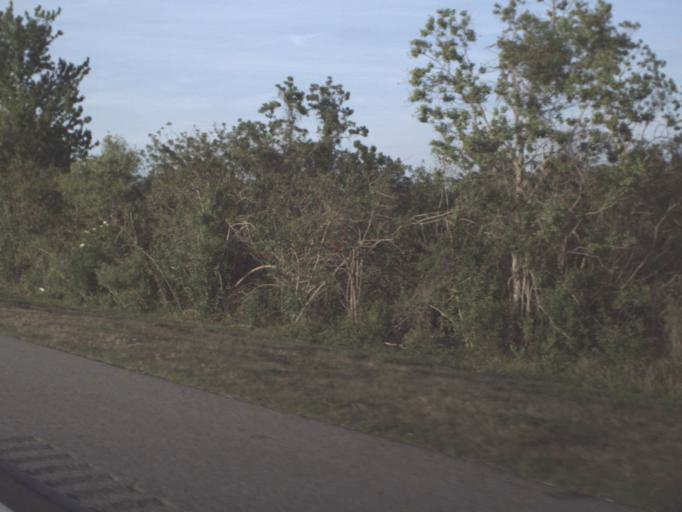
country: US
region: Florida
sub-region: Brevard County
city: Titusville
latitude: 28.5958
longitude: -80.8512
